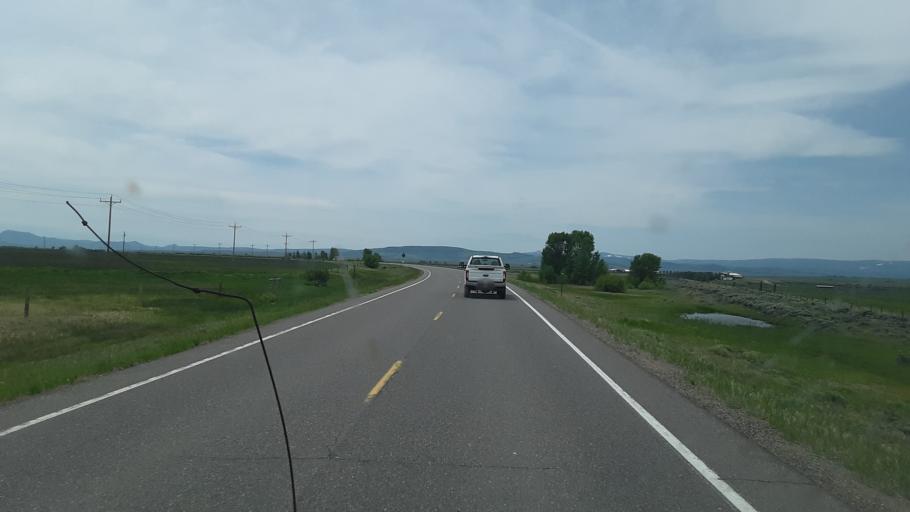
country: US
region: Colorado
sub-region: Jackson County
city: Walden
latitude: 40.6155
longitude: -106.4042
